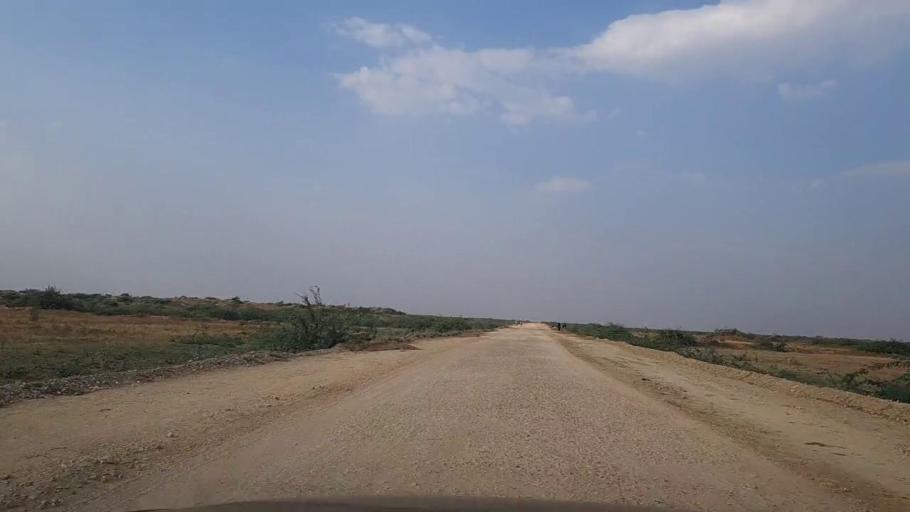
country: PK
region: Sindh
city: Gharo
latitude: 24.8308
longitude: 67.7454
